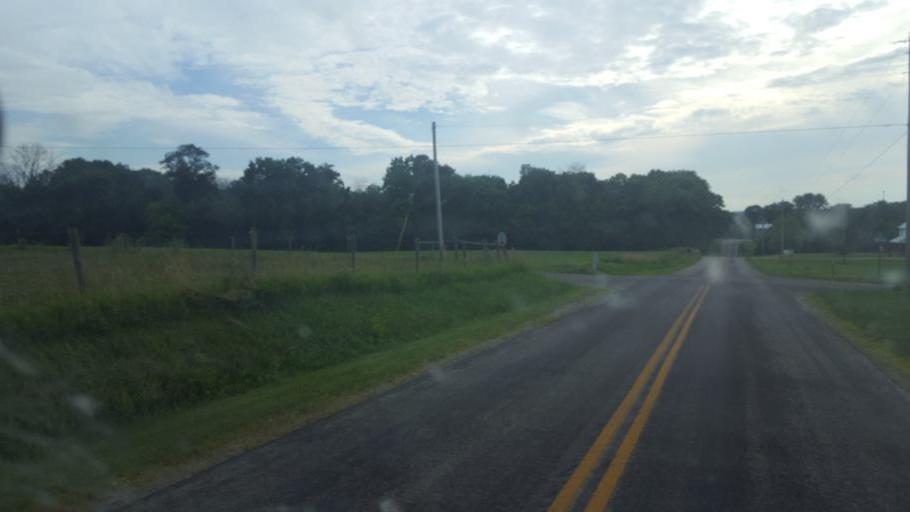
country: US
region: Ohio
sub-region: Ashland County
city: Loudonville
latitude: 40.7715
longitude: -82.1979
